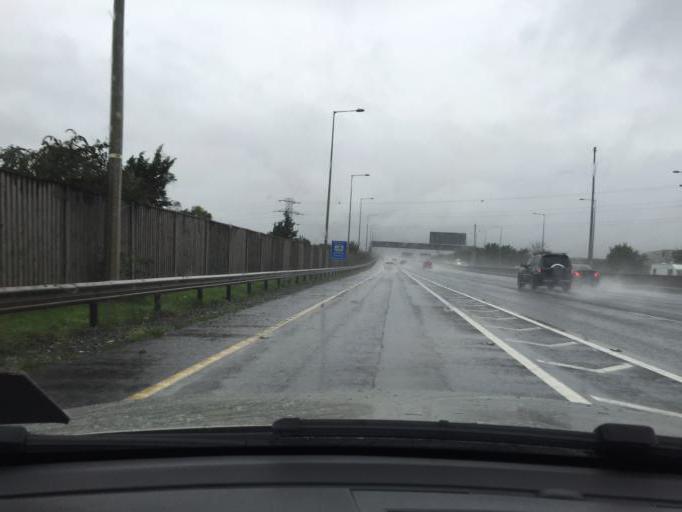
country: IE
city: Cherry Orchard
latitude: 53.3245
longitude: -6.3738
